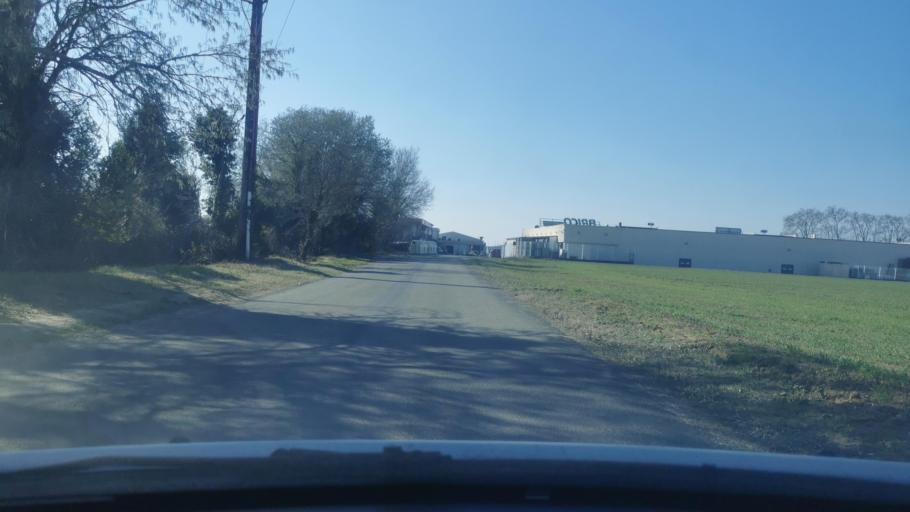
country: FR
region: Languedoc-Roussillon
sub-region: Departement du Gard
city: Montaren-et-Saint-Mediers
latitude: 44.0271
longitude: 4.3903
